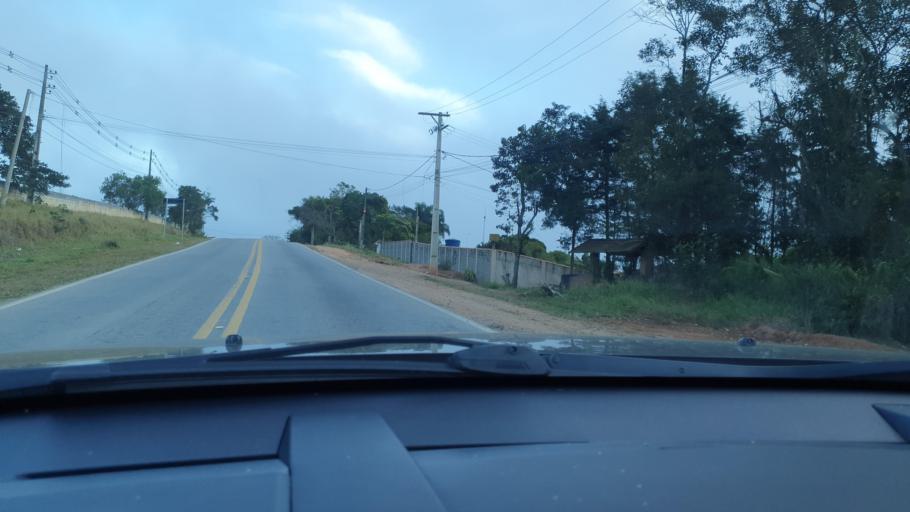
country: BR
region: Sao Paulo
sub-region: Ibiuna
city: Ibiuna
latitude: -23.6772
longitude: -47.2839
